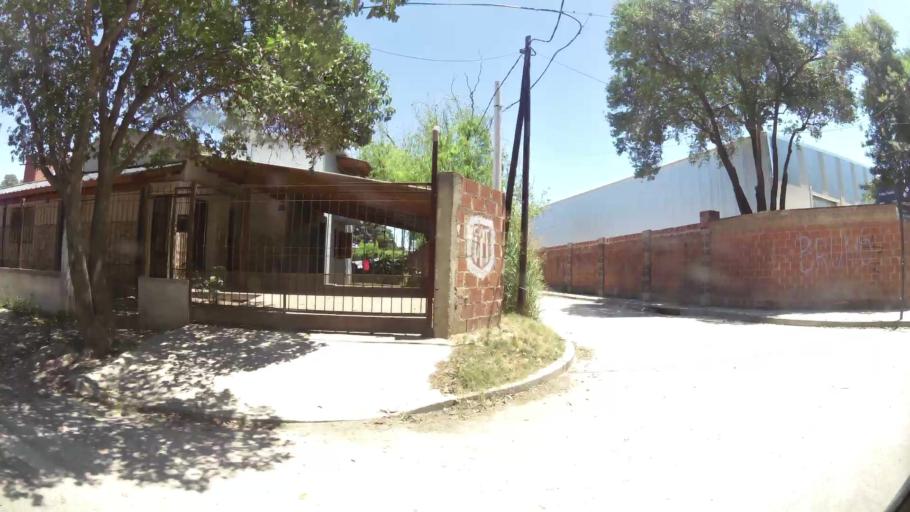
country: AR
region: Cordoba
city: Malvinas Argentinas
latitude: -31.3811
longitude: -64.1281
